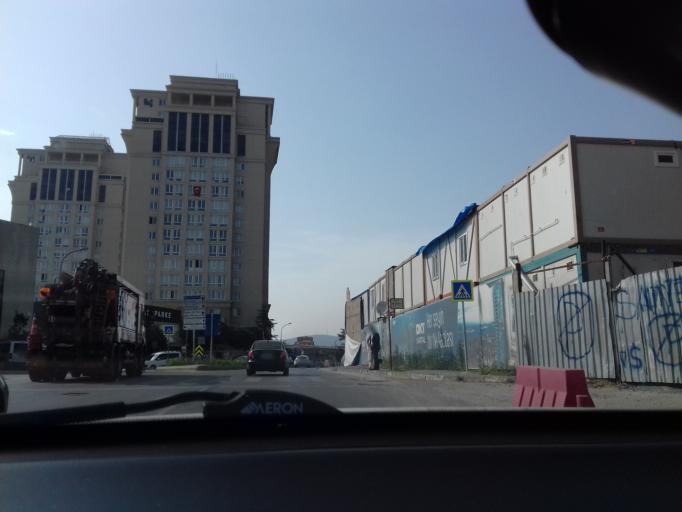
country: TR
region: Istanbul
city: Maltepe
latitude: 40.9094
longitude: 29.2124
